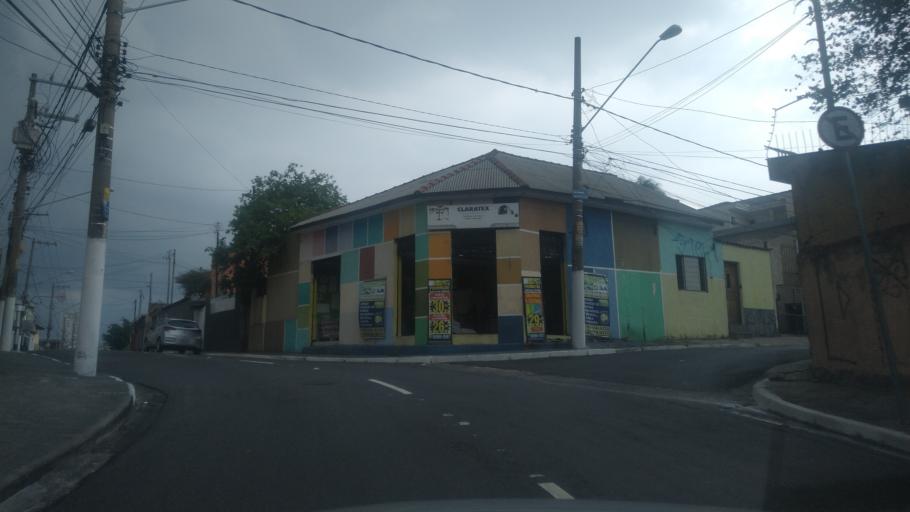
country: BR
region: Sao Paulo
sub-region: Sao Paulo
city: Sao Paulo
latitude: -23.4984
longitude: -46.6094
